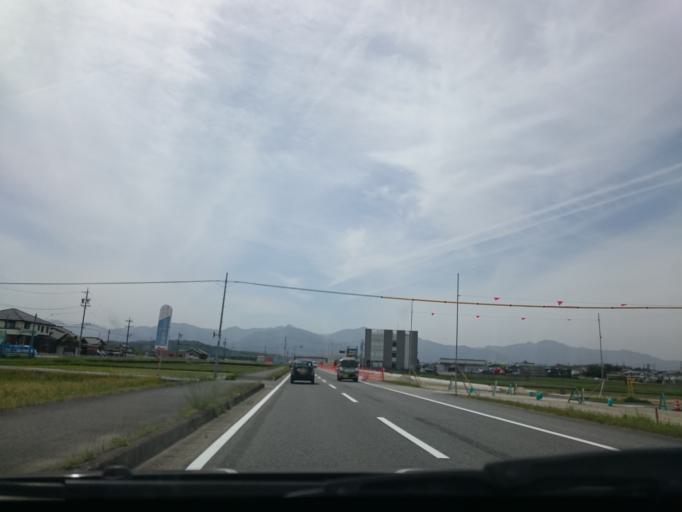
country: JP
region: Mie
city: Yokkaichi
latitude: 34.9816
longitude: 136.5744
